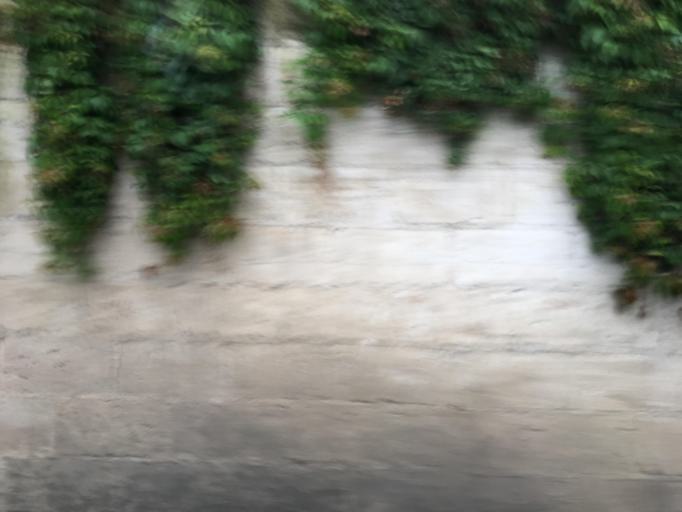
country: GT
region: Sacatepequez
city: Jocotenango
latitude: 14.5708
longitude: -90.7438
